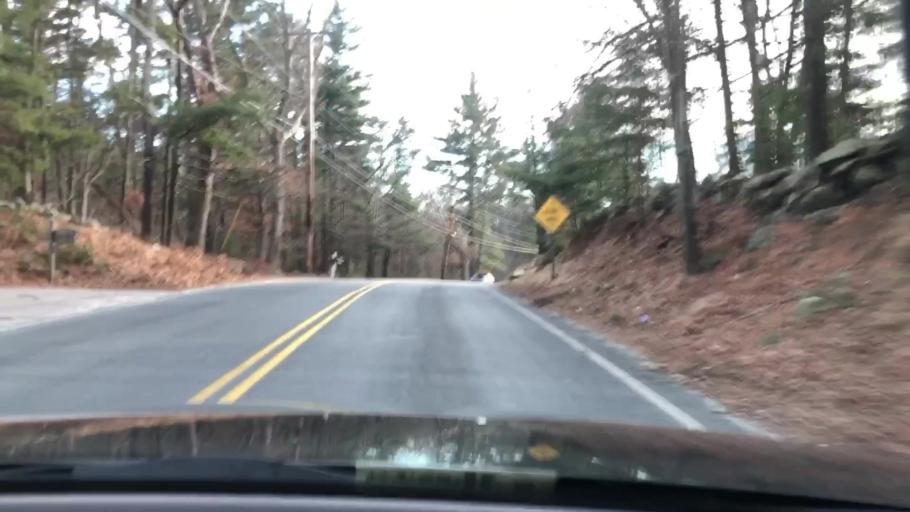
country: US
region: Massachusetts
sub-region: Worcester County
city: Mendon
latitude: 42.0706
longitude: -71.5246
